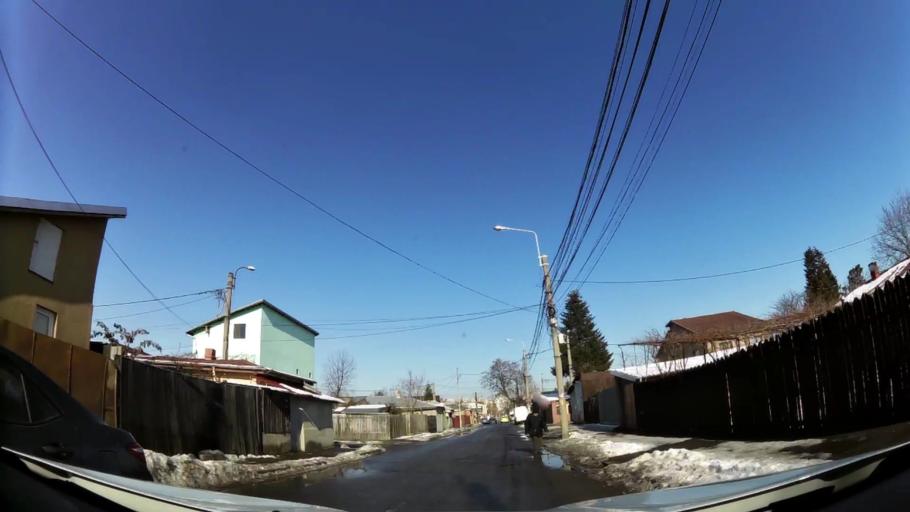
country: RO
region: Ilfov
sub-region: Comuna Magurele
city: Magurele
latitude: 44.3955
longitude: 26.0549
